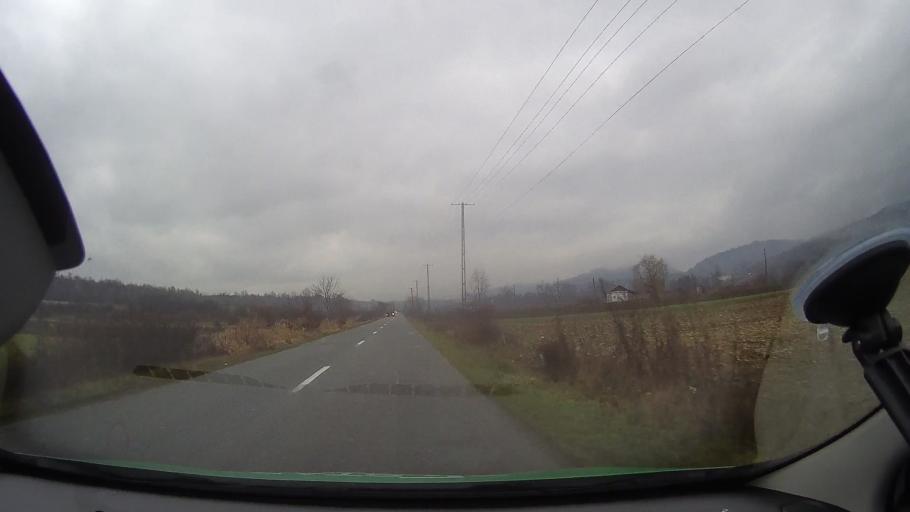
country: RO
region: Arad
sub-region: Comuna Brazii
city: Brazii
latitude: 46.2465
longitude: 22.3315
